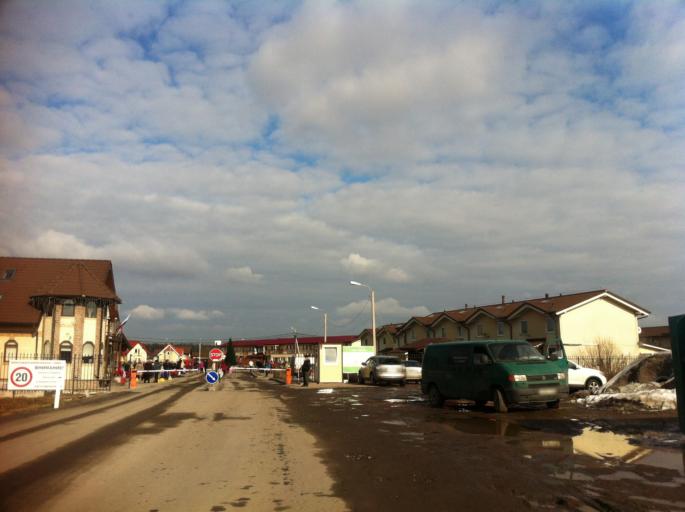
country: RU
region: Leningrad
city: Yanino Vtoroye
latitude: 59.9604
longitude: 30.5709
